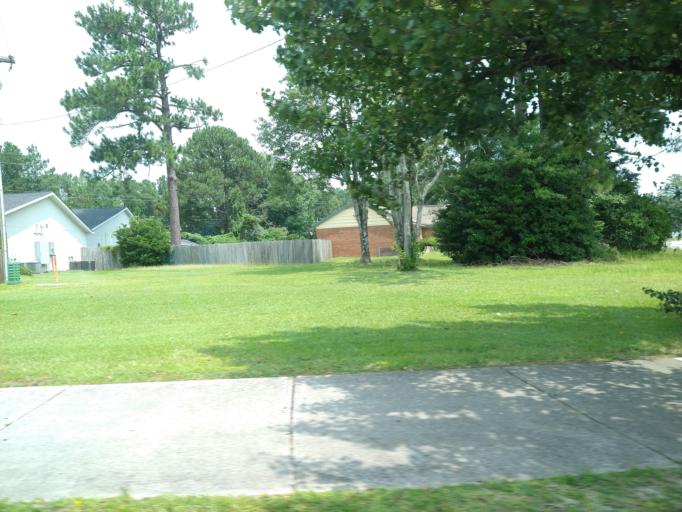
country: US
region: North Carolina
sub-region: Onslow County
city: Pumpkin Center
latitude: 34.7575
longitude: -77.3815
